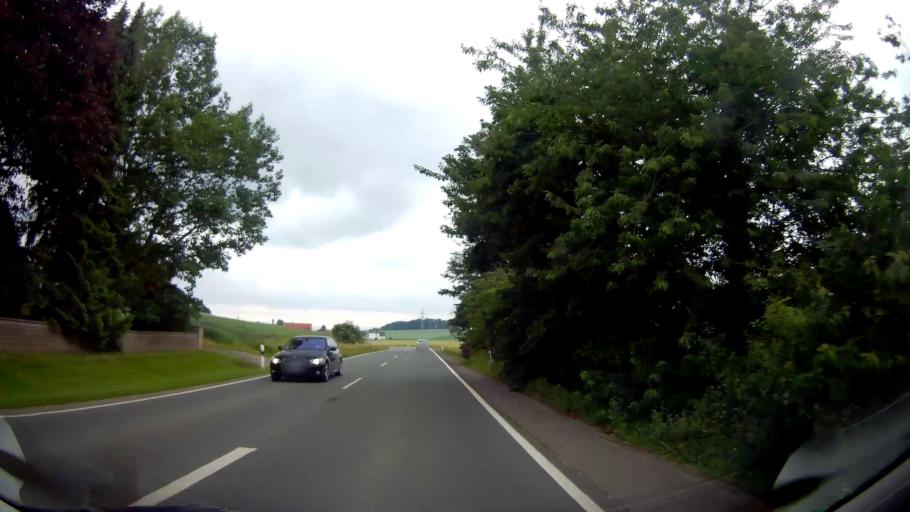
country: DE
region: North Rhine-Westphalia
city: Loehne
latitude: 52.1466
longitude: 8.7042
